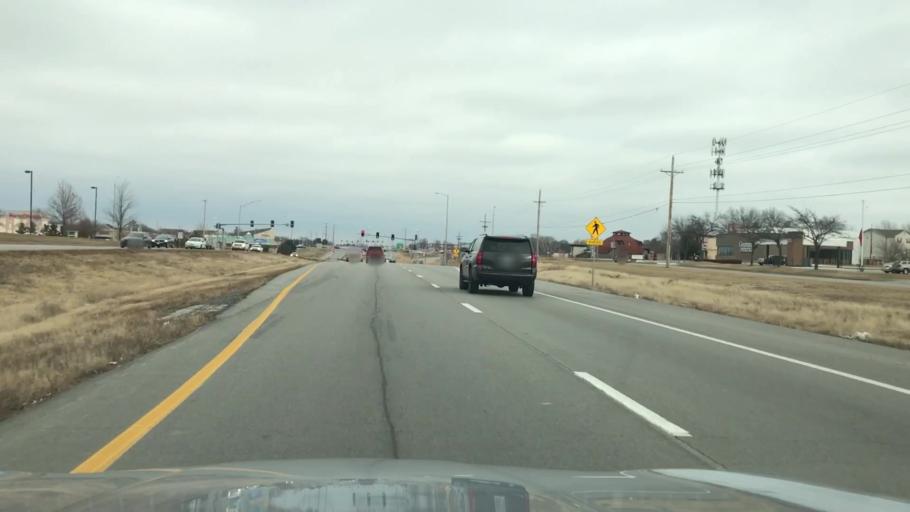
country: US
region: Missouri
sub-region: Jackson County
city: Lees Summit
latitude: 38.9259
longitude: -94.3601
